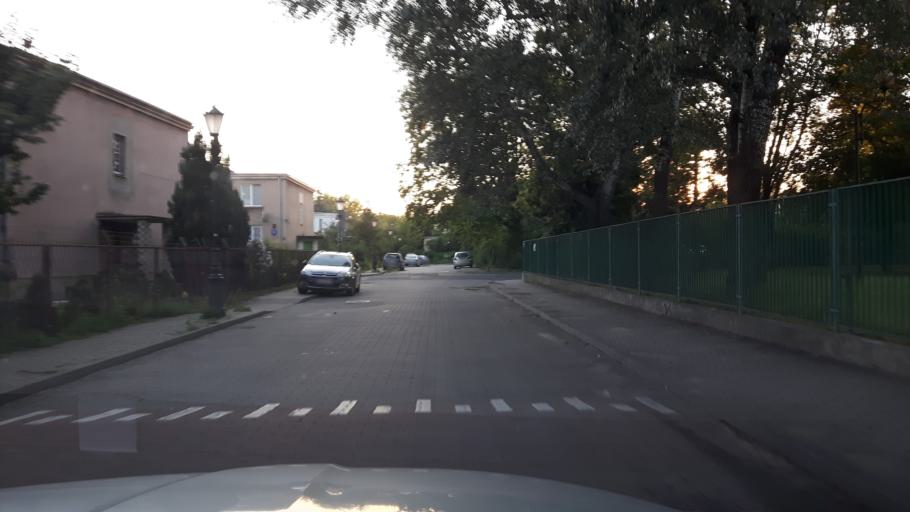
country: PL
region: Masovian Voivodeship
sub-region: Warszawa
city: Wilanow
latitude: 52.1869
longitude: 21.0707
